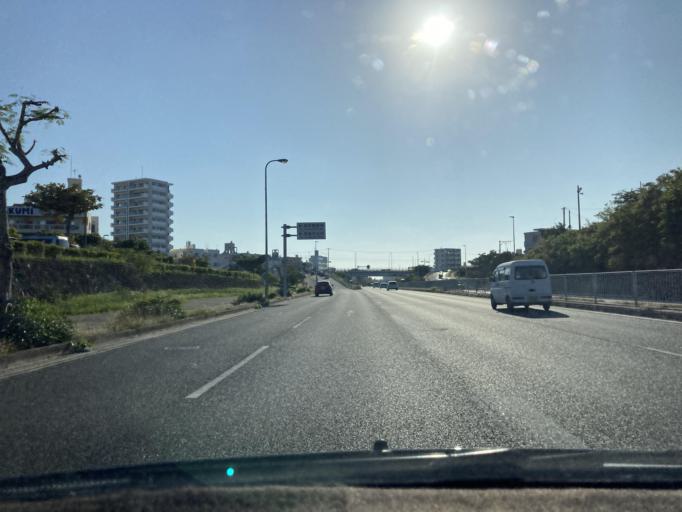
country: JP
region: Okinawa
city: Ginowan
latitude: 26.2509
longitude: 127.7191
